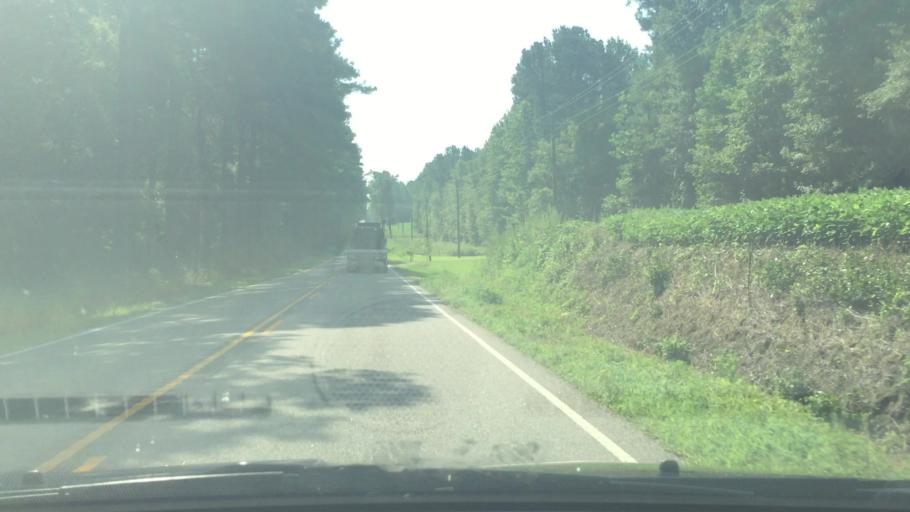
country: US
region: Virginia
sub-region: Sussex County
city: Sussex
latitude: 37.0335
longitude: -77.3034
